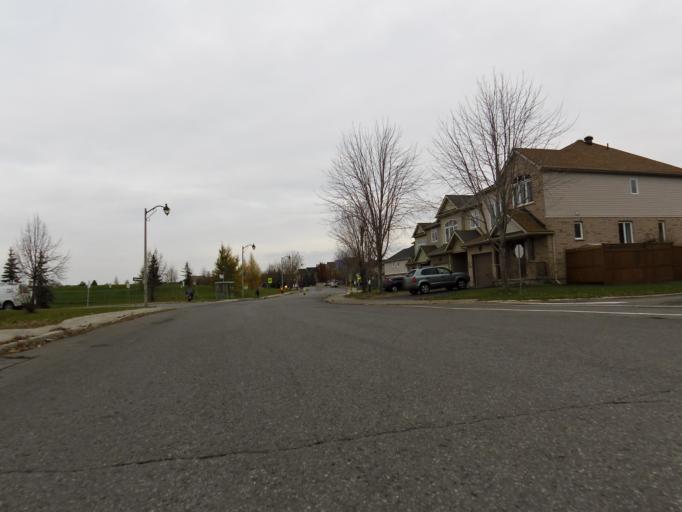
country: CA
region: Ontario
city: Bells Corners
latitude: 45.2822
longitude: -75.7078
